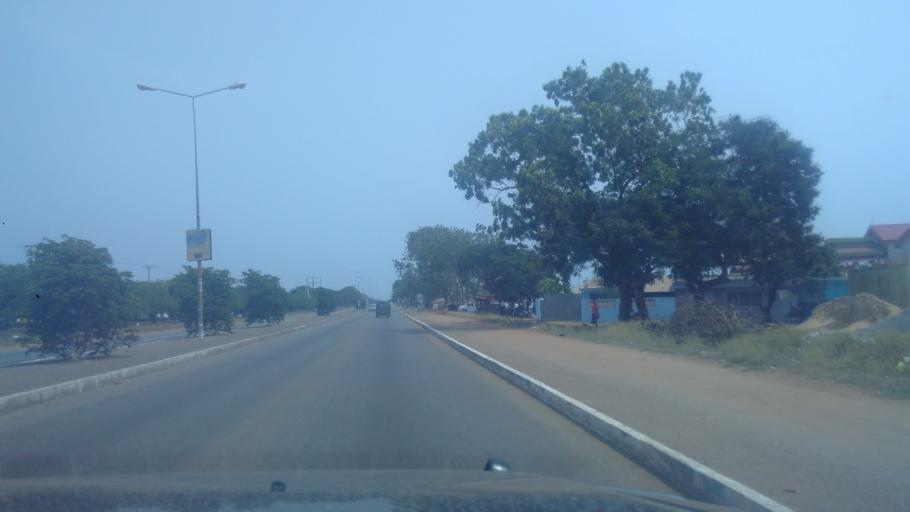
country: GH
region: Greater Accra
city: Tema
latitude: 5.6807
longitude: -0.0129
